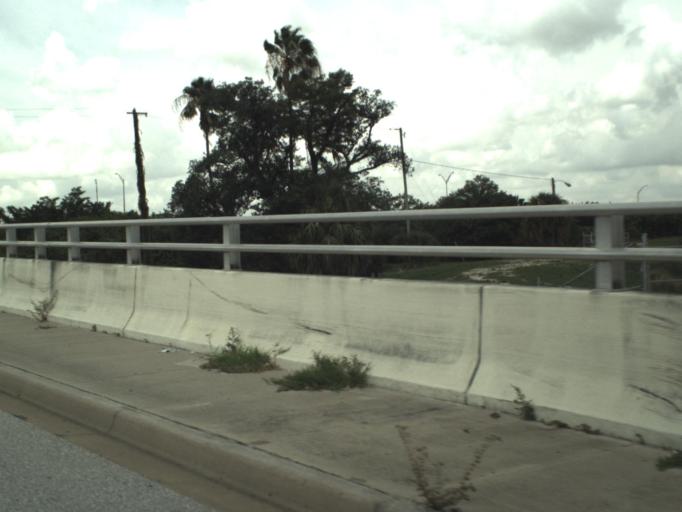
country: US
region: Florida
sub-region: Palm Beach County
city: West Palm Beach
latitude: 26.7010
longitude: -80.0699
